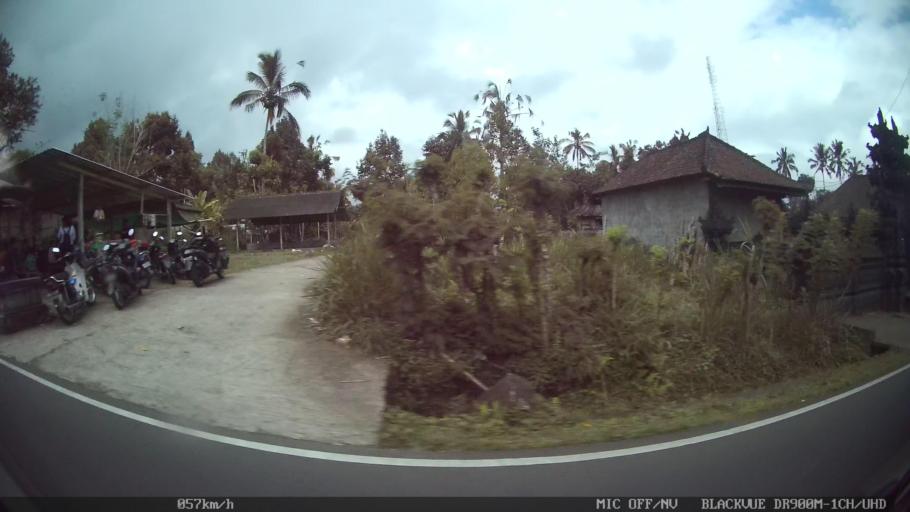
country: ID
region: Bali
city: Banjar Tiga
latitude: -8.3843
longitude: 115.4177
